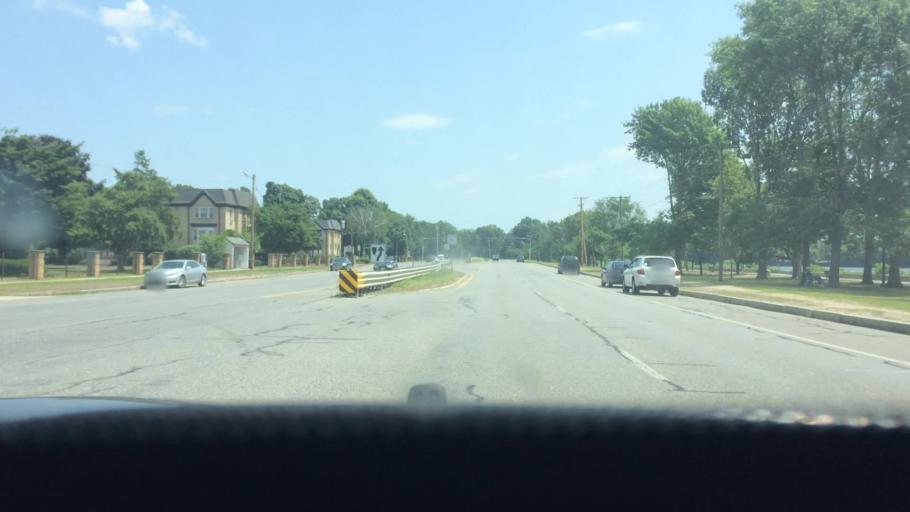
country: US
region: Massachusetts
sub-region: Middlesex County
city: Lowell
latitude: 42.6413
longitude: -71.3474
